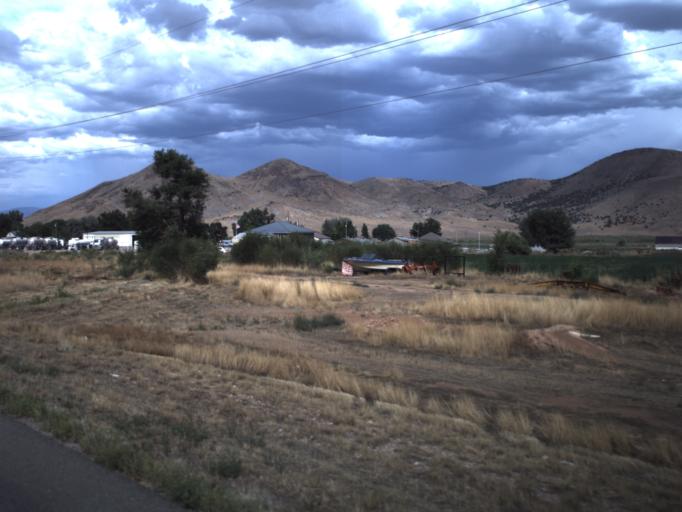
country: US
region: Utah
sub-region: Sevier County
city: Aurora
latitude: 38.8583
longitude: -111.9705
